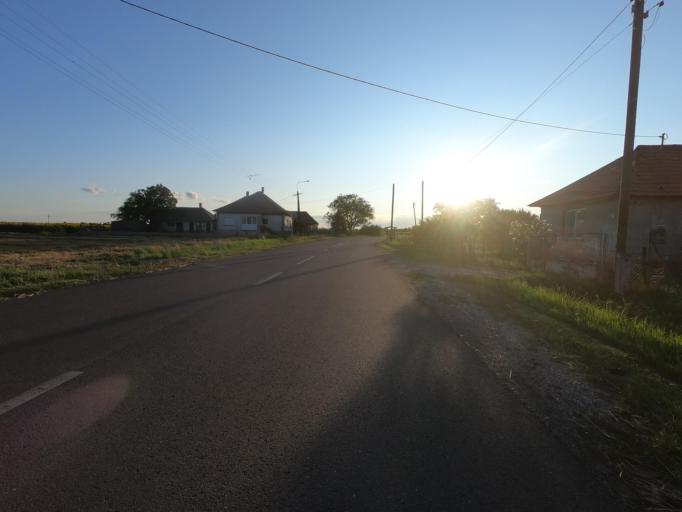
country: HU
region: Heves
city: Besenyotelek
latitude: 47.7242
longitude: 20.4671
